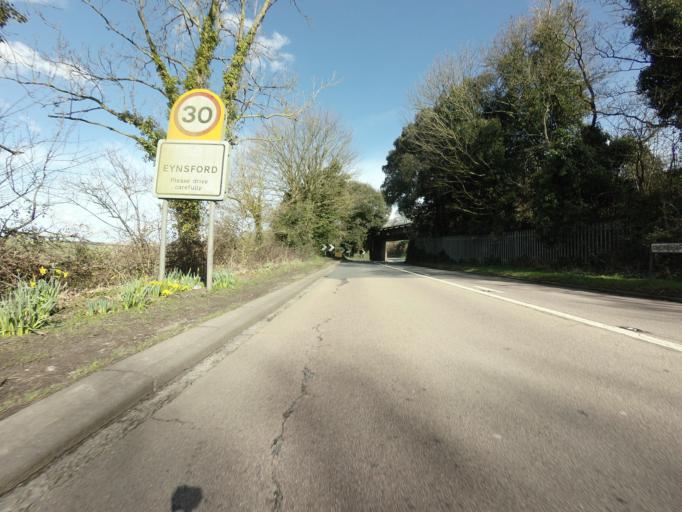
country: GB
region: England
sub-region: Kent
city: Eynsford
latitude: 51.3628
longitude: 0.2039
